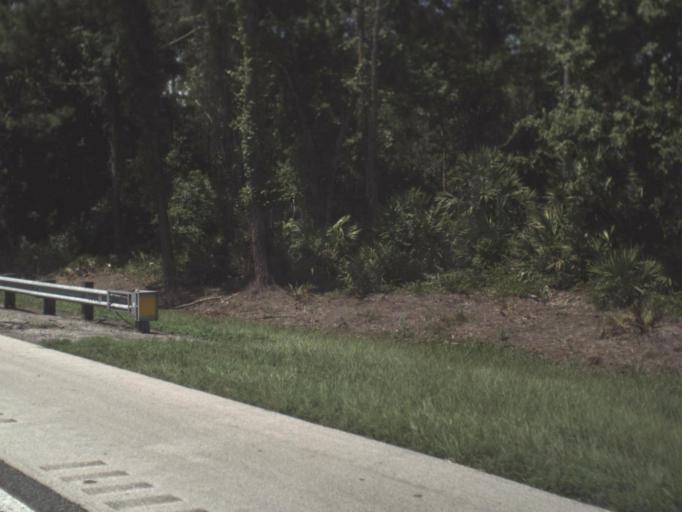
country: US
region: Florida
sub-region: Saint Johns County
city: Saint Augustine South
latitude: 29.8625
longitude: -81.3955
